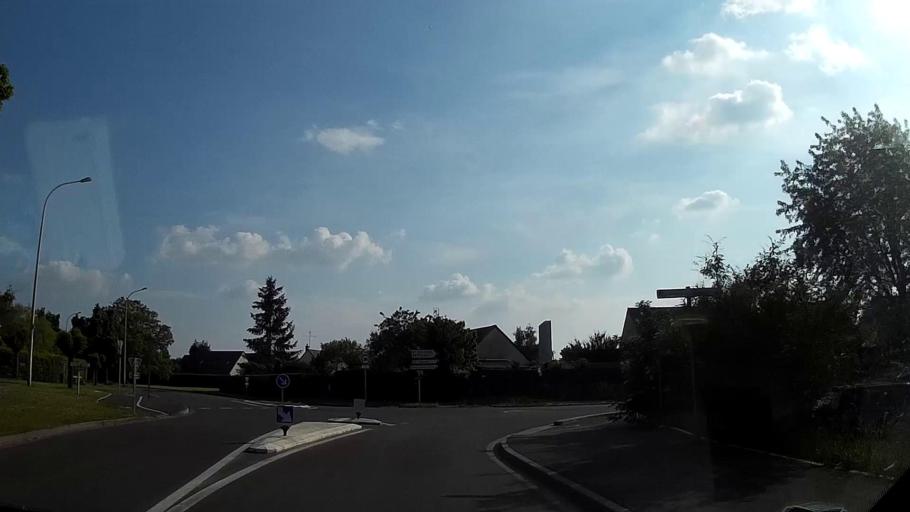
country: FR
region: Centre
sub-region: Departement du Loir-et-Cher
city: Saint-Sulpice-de-Pommeray
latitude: 47.5987
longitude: 1.2995
